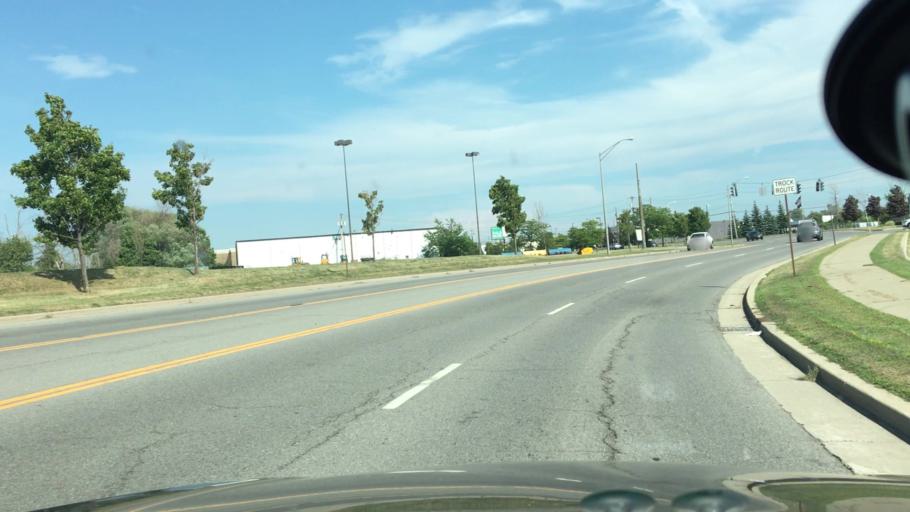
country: US
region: New York
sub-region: Erie County
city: Cheektowaga
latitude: 42.9170
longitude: -78.7588
